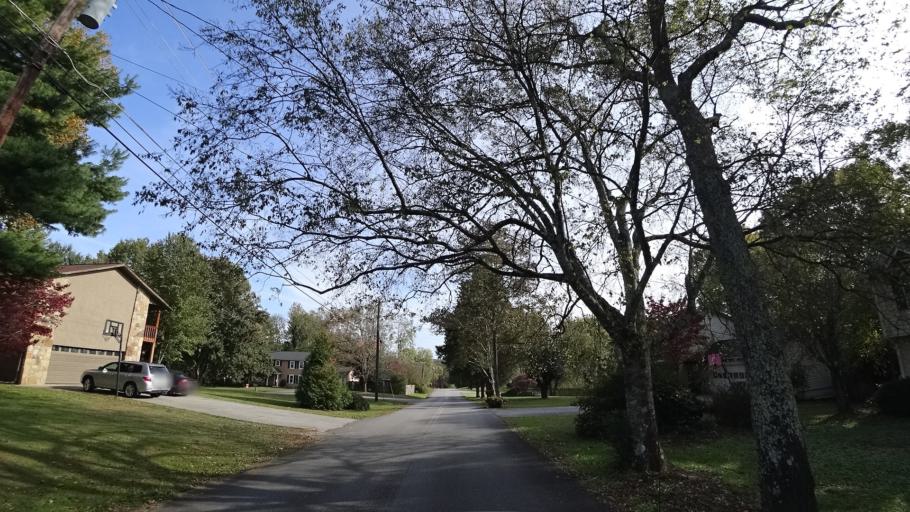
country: US
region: Tennessee
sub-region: Knox County
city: Farragut
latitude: 35.9085
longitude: -84.1618
